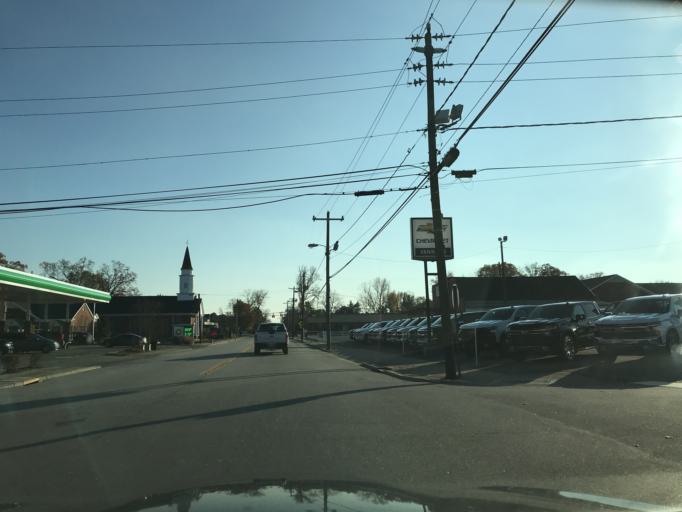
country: US
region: North Carolina
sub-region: Granville County
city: Creedmoor
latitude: 36.1182
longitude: -78.6868
